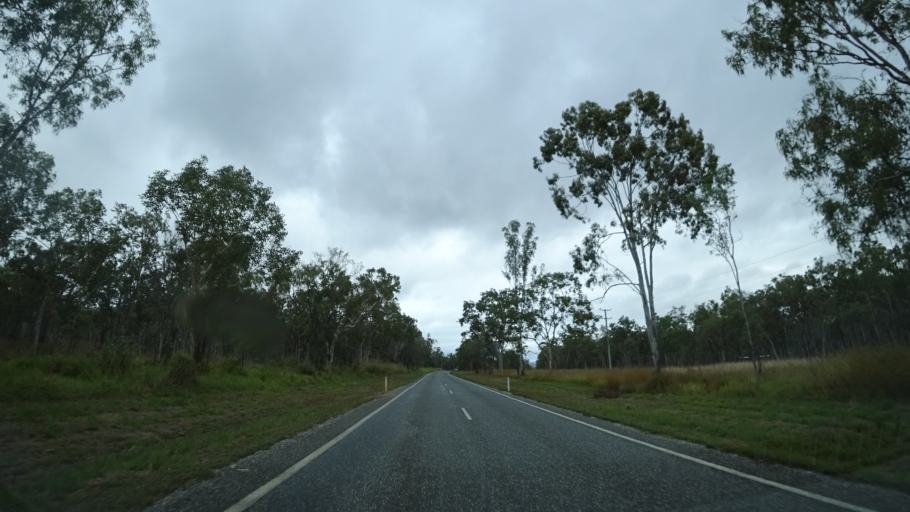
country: AU
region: Queensland
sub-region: Cairns
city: Port Douglas
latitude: -16.7262
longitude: 145.3528
